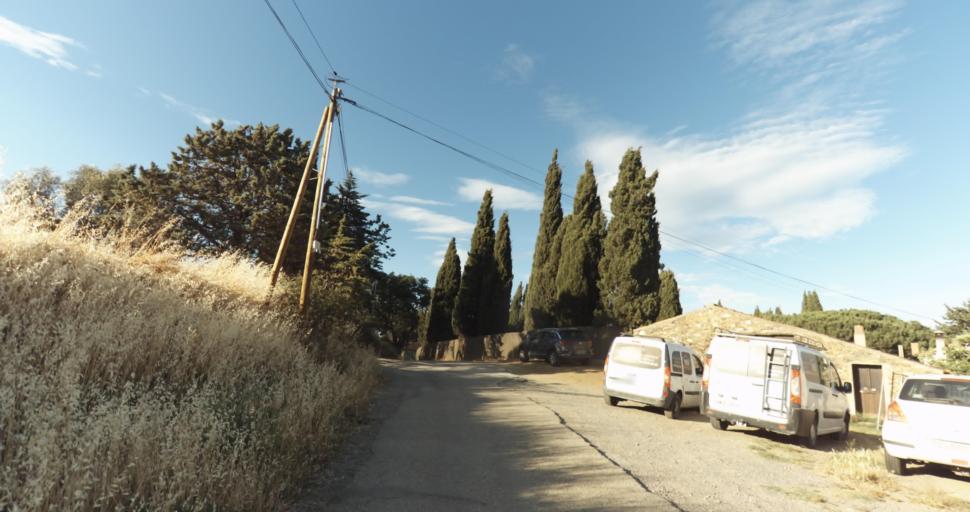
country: FR
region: Provence-Alpes-Cote d'Azur
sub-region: Departement du Var
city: La Croix-Valmer
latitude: 43.2150
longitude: 6.5643
